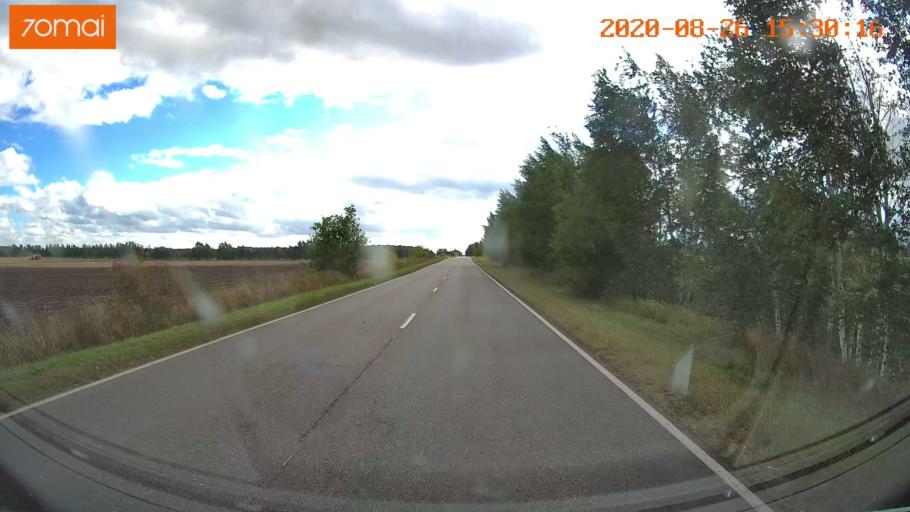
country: RU
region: Tula
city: Severo-Zadonsk
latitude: 54.0933
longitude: 38.3988
